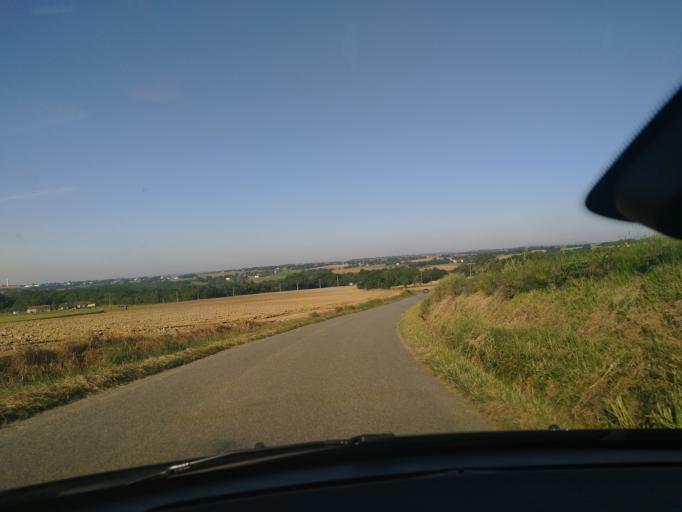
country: FR
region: Midi-Pyrenees
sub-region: Departement du Gers
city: Gimont
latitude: 43.7508
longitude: 0.9167
